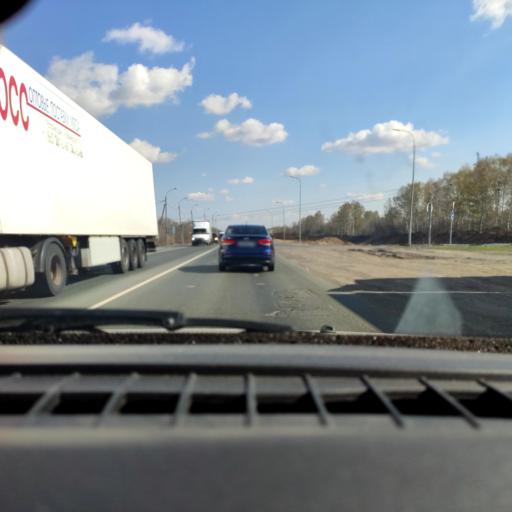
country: RU
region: Samara
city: Krasnyy Yar
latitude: 53.4528
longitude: 50.3858
